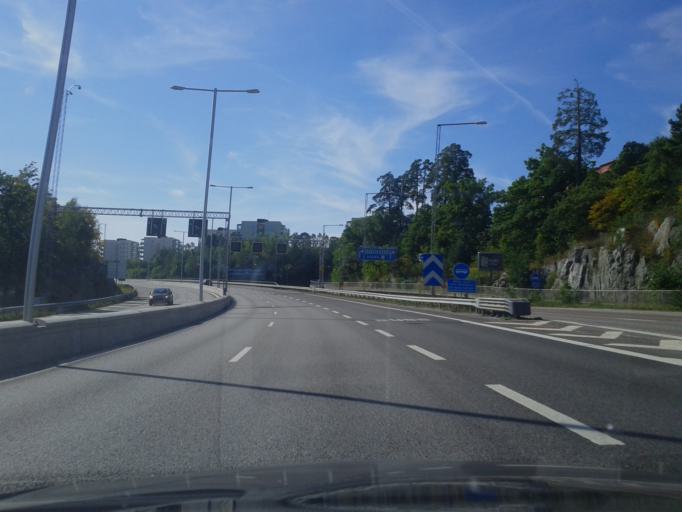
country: SE
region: Stockholm
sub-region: Norrtalje Kommun
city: Bergshamra
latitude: 59.3820
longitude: 18.0410
